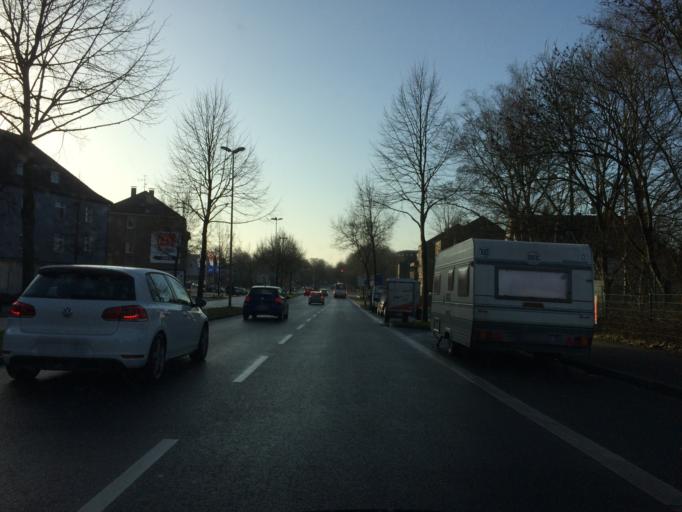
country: DE
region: North Rhine-Westphalia
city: Bochum-Hordel
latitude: 51.5263
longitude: 7.1884
